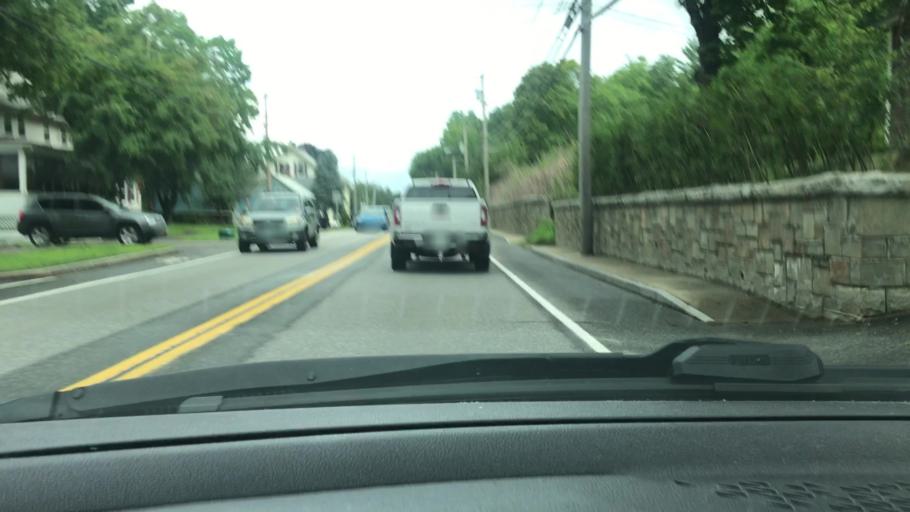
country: US
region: New Hampshire
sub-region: Merrimack County
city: East Concord
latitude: 43.2420
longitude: -71.5691
